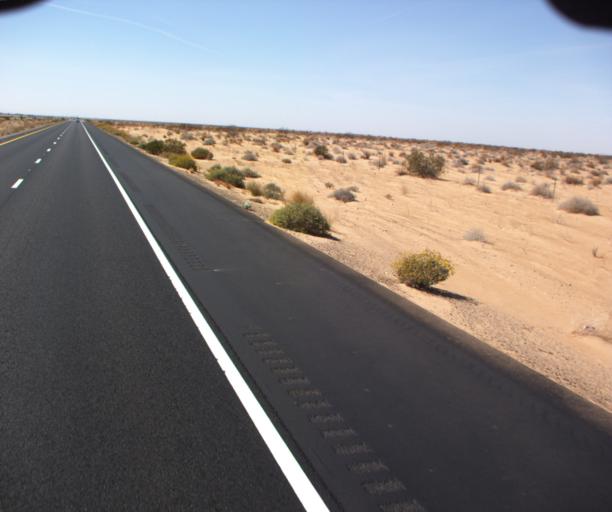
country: US
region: Arizona
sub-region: Yuma County
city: Somerton
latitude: 32.4954
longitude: -114.6039
